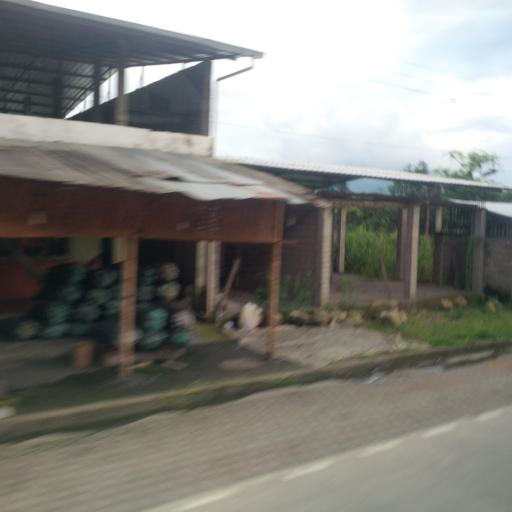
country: EC
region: Chimborazo
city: Alausi
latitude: -2.1994
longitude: -79.1180
